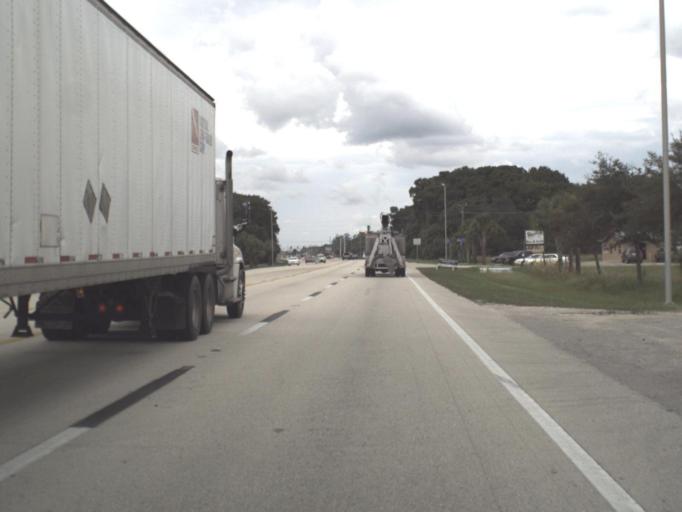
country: US
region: Florida
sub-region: Lee County
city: Fort Myers Shores
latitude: 26.7031
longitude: -81.7546
